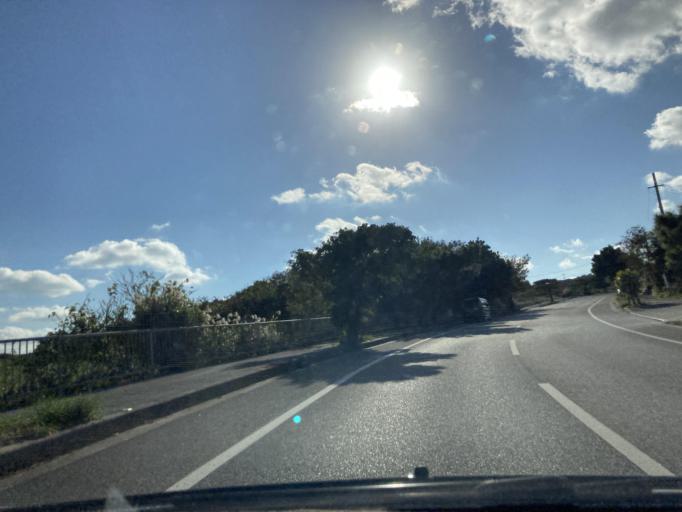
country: JP
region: Okinawa
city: Katsuren-haebaru
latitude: 26.3055
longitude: 127.9207
